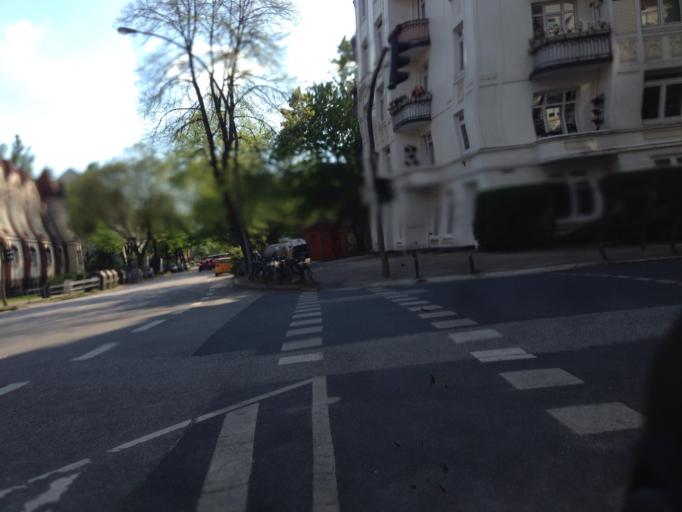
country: DE
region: Hamburg
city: Hamburg
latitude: 53.5779
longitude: 10.0276
